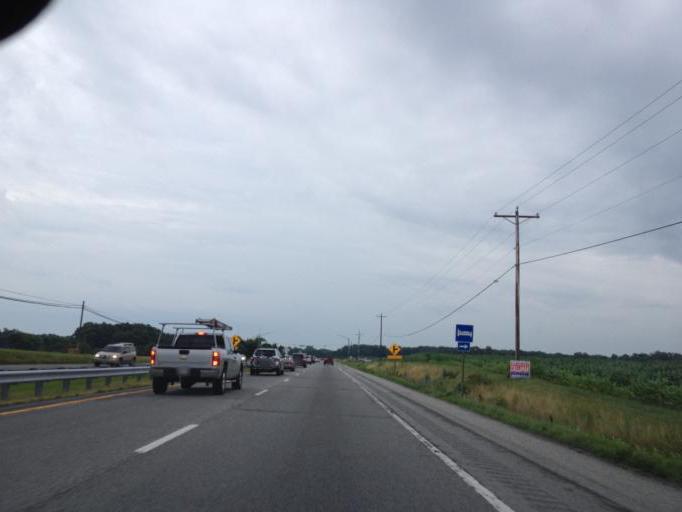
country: US
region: Maryland
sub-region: Queen Anne's County
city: Grasonville
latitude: 38.9709
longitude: -76.1217
